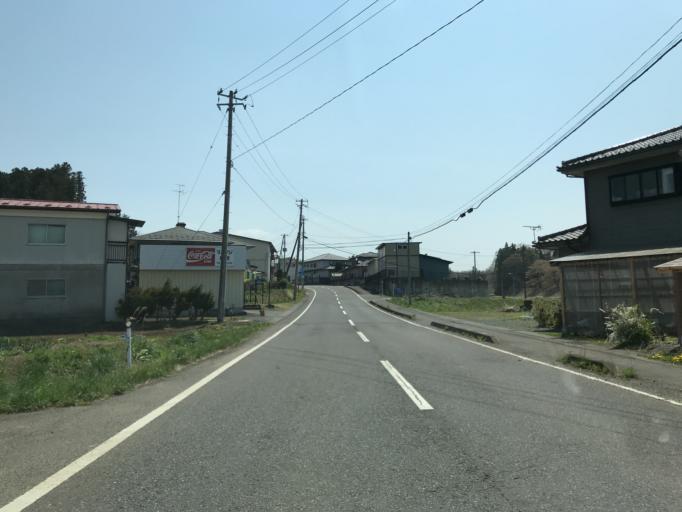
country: JP
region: Fukushima
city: Ishikawa
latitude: 37.1090
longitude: 140.3870
